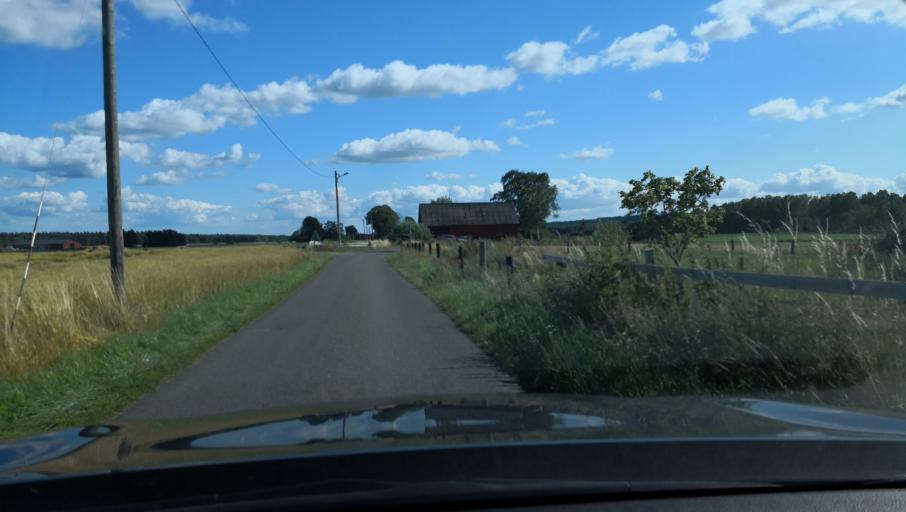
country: SE
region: Skane
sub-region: Kristianstads Kommun
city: Degeberga
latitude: 55.8144
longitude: 14.1889
